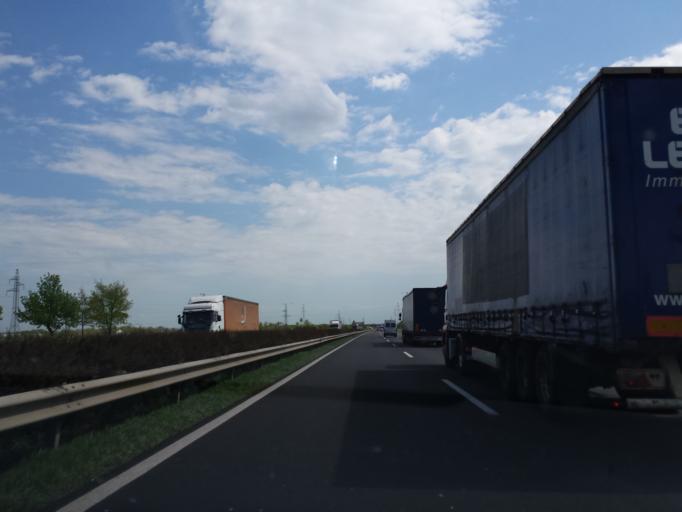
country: HU
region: Gyor-Moson-Sopron
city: Mosonmagyarovar
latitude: 47.8572
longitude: 17.2412
